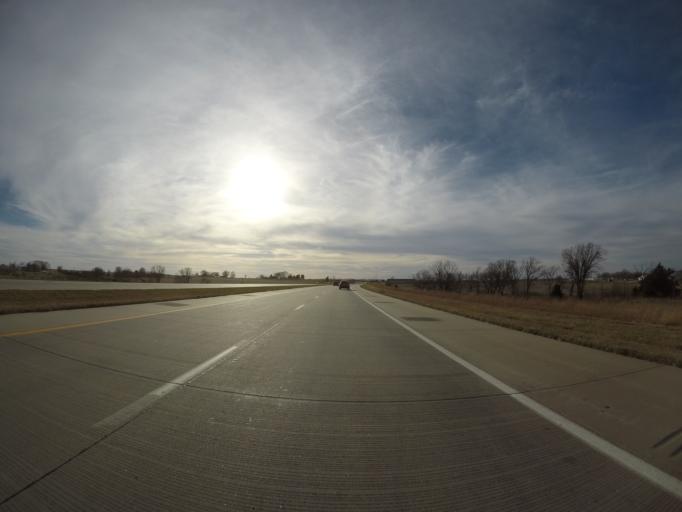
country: US
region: Kansas
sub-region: Franklin County
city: Ottawa
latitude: 38.5844
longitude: -95.2432
